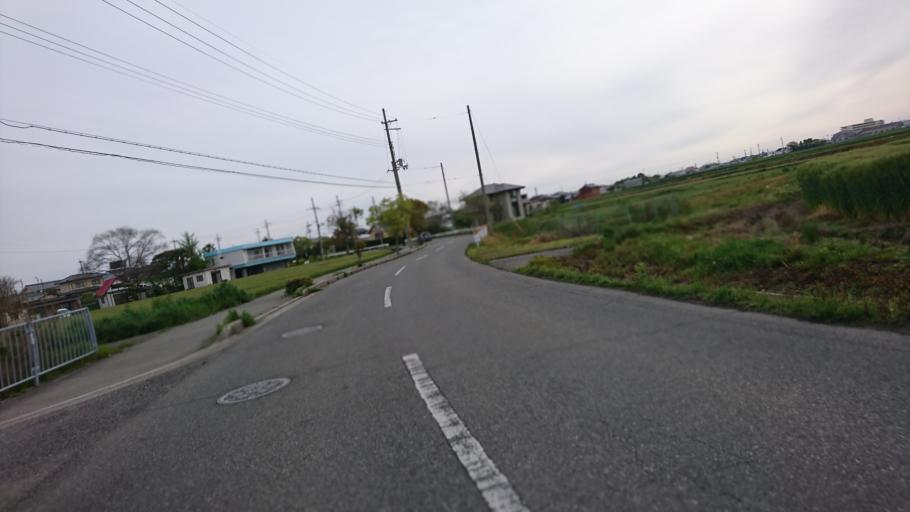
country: JP
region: Hyogo
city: Kakogawacho-honmachi
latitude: 34.7581
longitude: 134.9073
